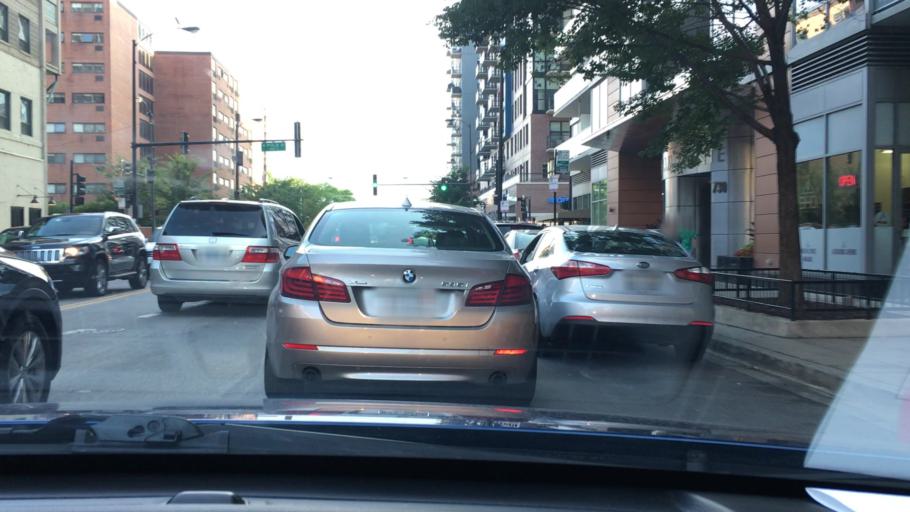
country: US
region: Illinois
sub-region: Cook County
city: Chicago
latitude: 41.8728
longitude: -87.6307
